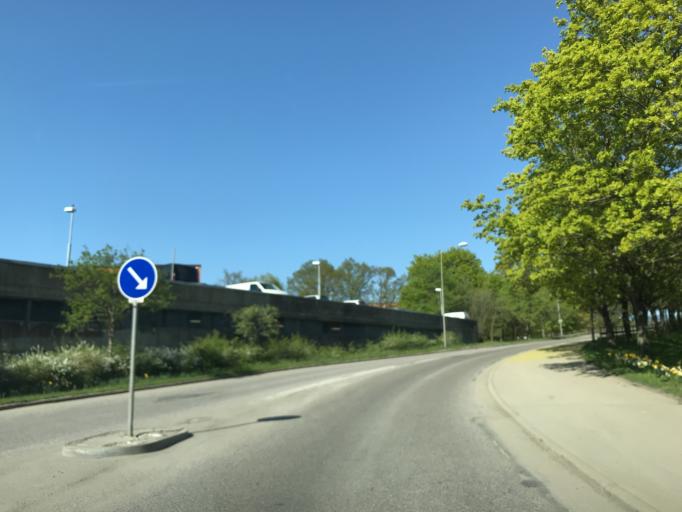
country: SE
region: Stockholm
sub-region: Stockholms Kommun
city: Arsta
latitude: 59.2820
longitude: 18.0146
